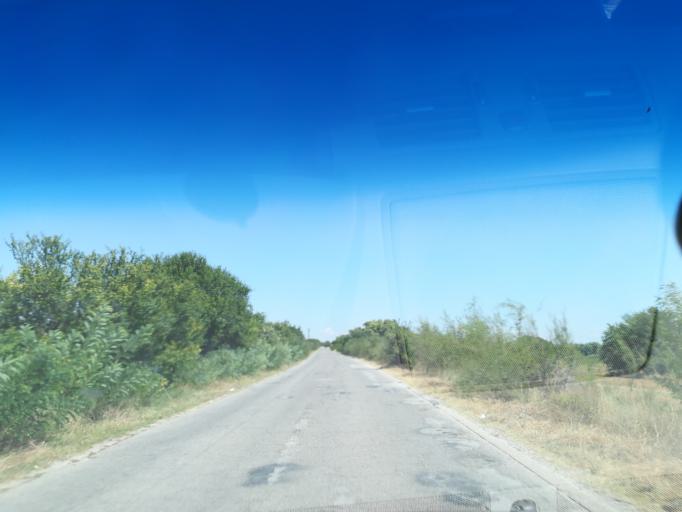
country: BG
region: Plovdiv
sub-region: Obshtina Sadovo
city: Sadovo
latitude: 42.0242
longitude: 24.9960
